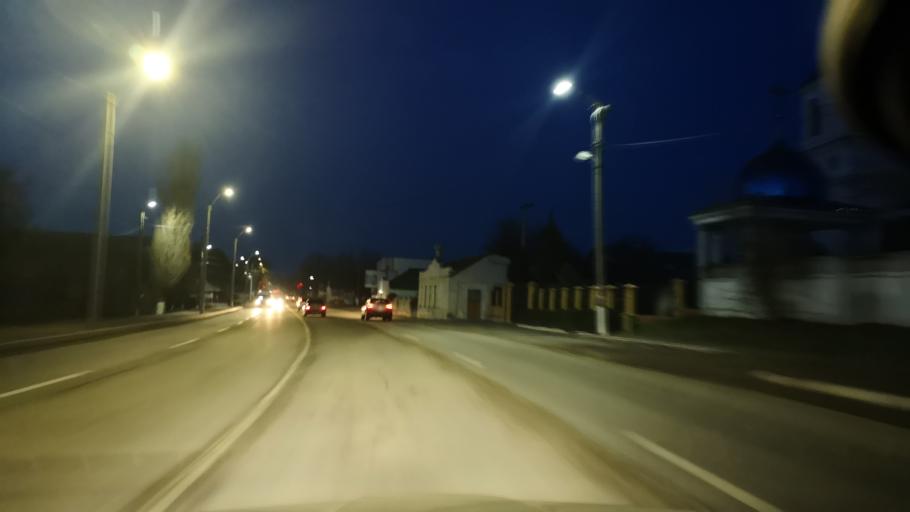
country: MD
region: Orhei
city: Orhei
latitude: 47.3566
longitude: 28.8128
